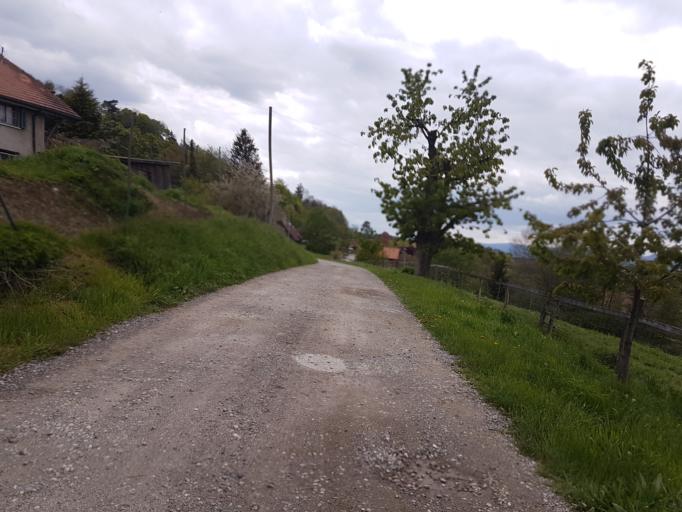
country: CH
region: Bern
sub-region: Seeland District
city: Leuzigen
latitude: 47.1749
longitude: 7.4740
